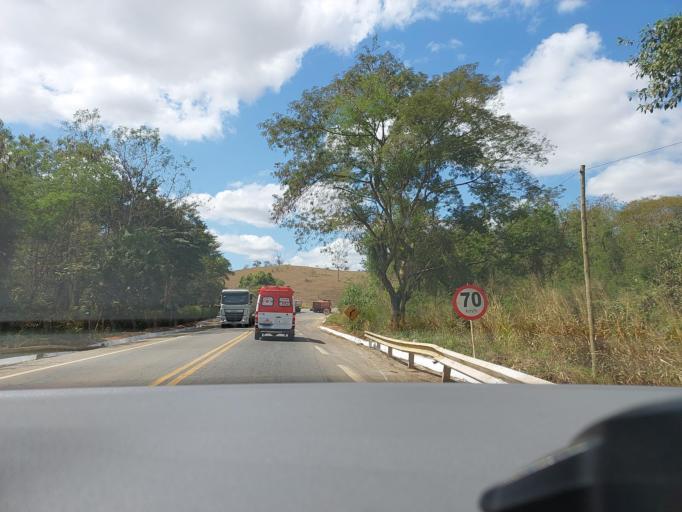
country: BR
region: Minas Gerais
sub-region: Muriae
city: Muriae
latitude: -21.1264
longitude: -42.3315
